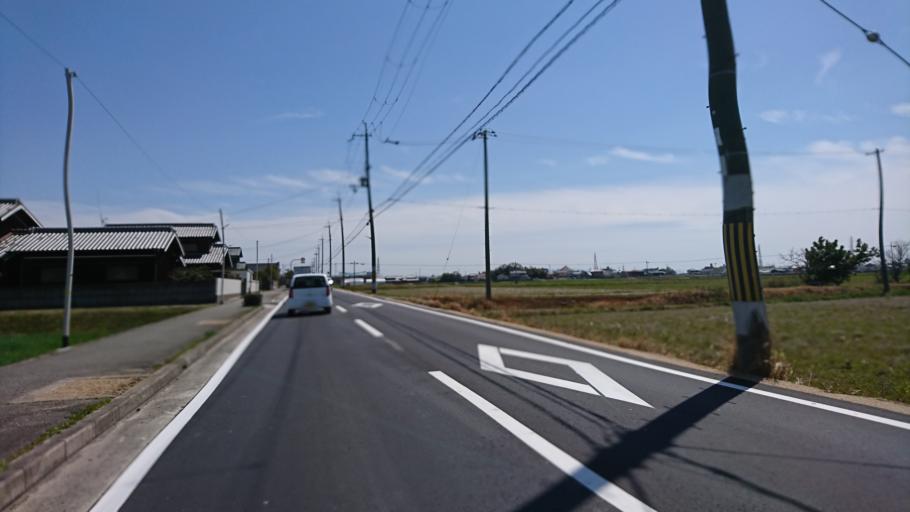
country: JP
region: Hyogo
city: Kakogawacho-honmachi
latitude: 34.7387
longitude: 134.8952
